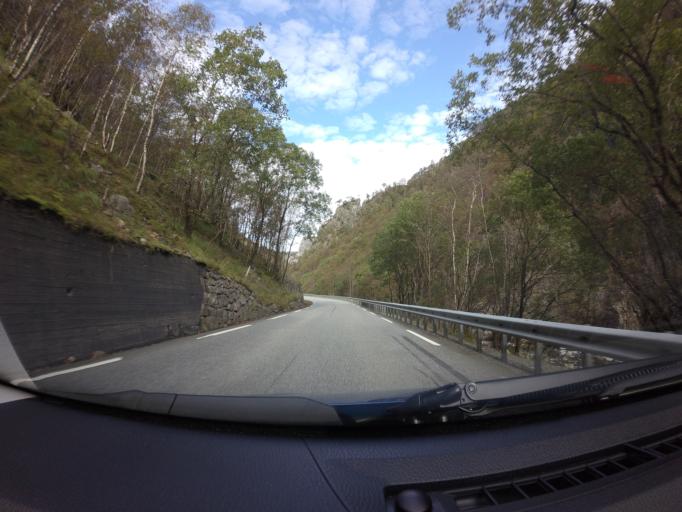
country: NO
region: Rogaland
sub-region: Forsand
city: Forsand
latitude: 58.7903
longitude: 6.2792
